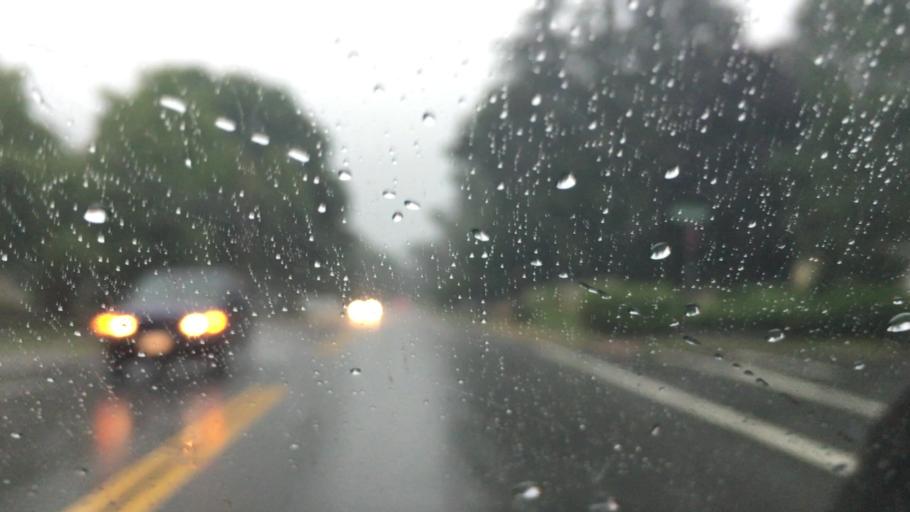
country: US
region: Massachusetts
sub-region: Middlesex County
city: Lexington
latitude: 42.4403
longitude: -71.1925
